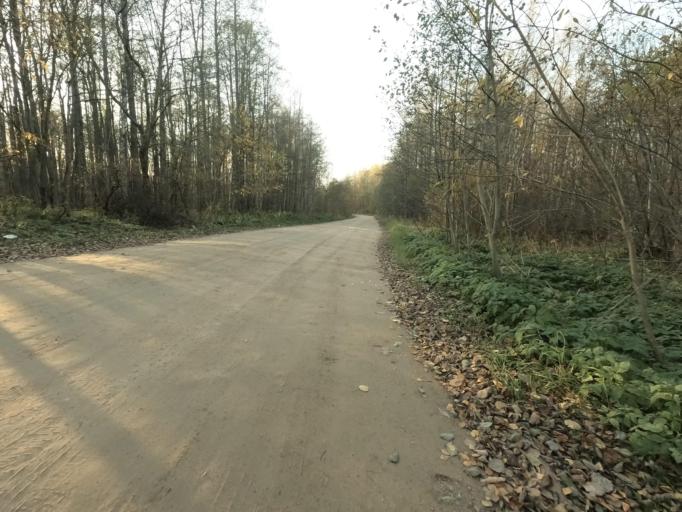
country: RU
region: Leningrad
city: Sinyavino
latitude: 59.8782
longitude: 31.0394
